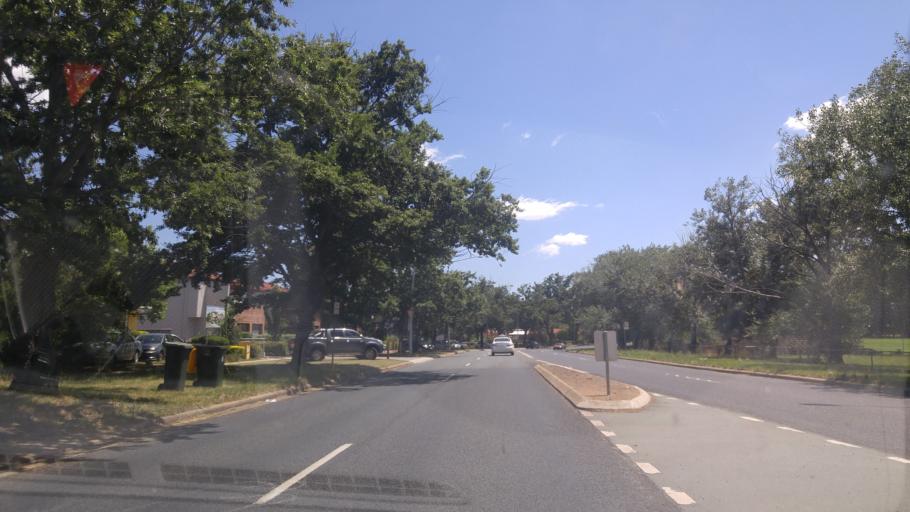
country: AU
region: Australian Capital Territory
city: Canberra
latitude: -35.2602
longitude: 149.1364
